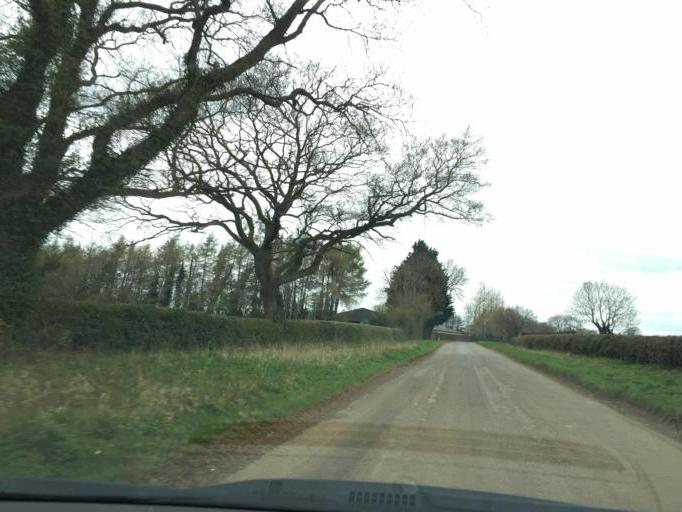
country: GB
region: England
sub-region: Oxfordshire
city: Hanwell
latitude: 52.0966
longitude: -1.3989
